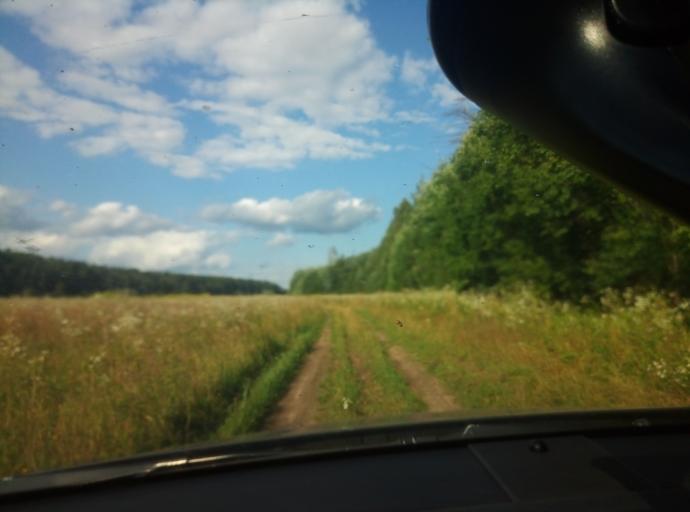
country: RU
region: Kaluga
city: Yukhnov
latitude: 54.7316
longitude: 35.1208
